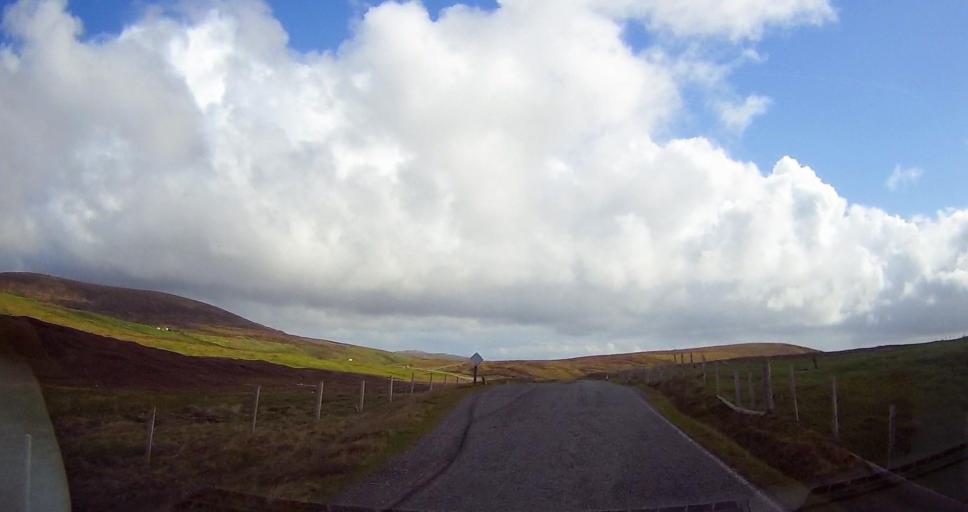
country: GB
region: Scotland
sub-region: Shetland Islands
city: Lerwick
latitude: 60.5135
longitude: -1.3832
